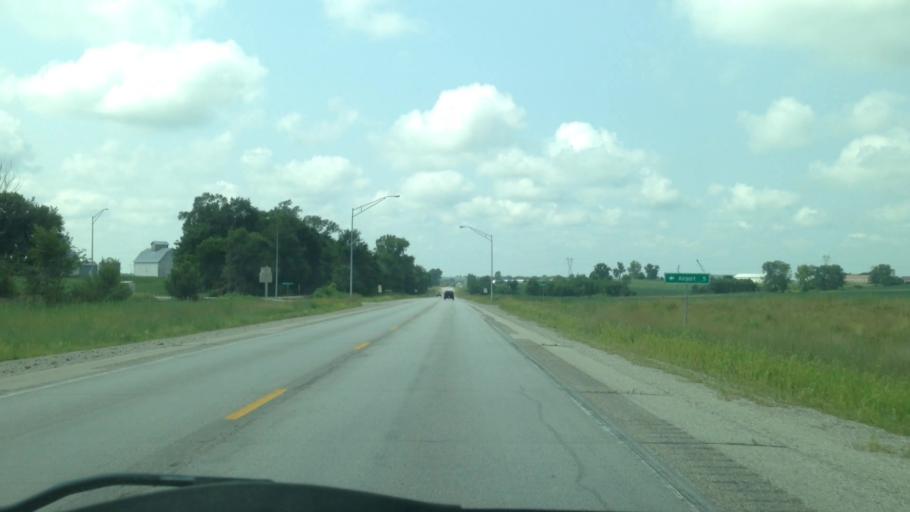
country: US
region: Iowa
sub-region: Benton County
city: Walford
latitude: 41.8941
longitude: -91.8126
